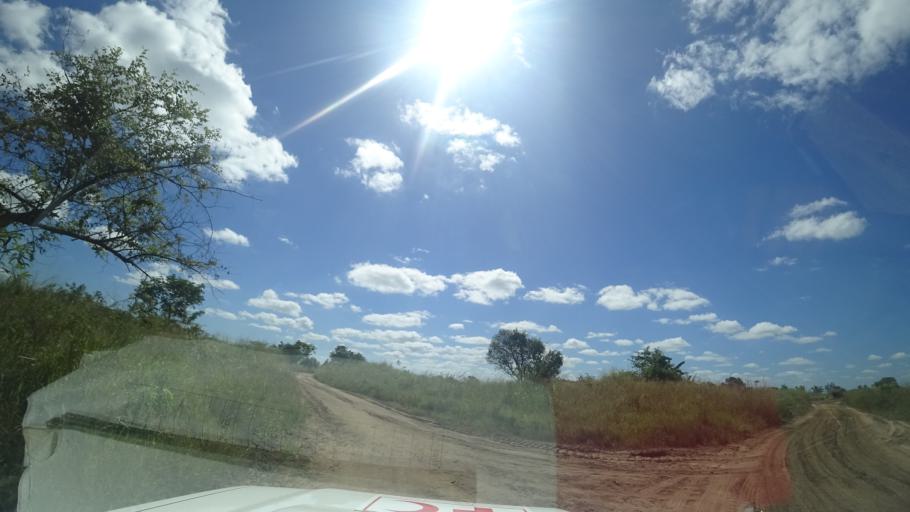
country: MZ
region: Sofala
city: Dondo
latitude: -19.4598
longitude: 34.5946
